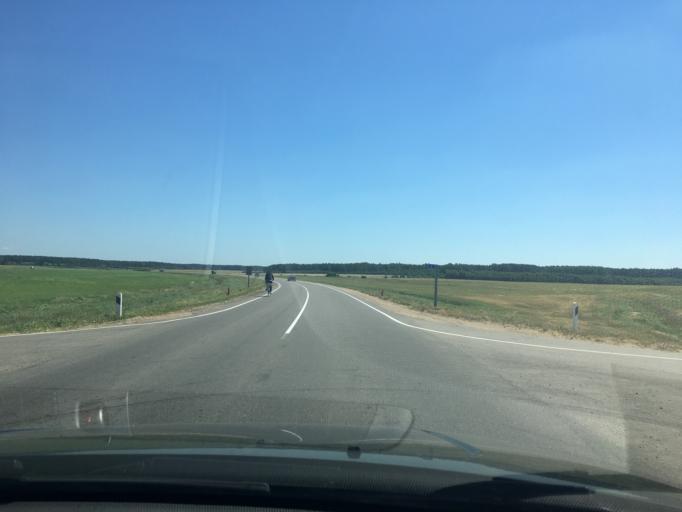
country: BY
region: Grodnenskaya
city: Iwye
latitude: 53.9128
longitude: 25.7733
